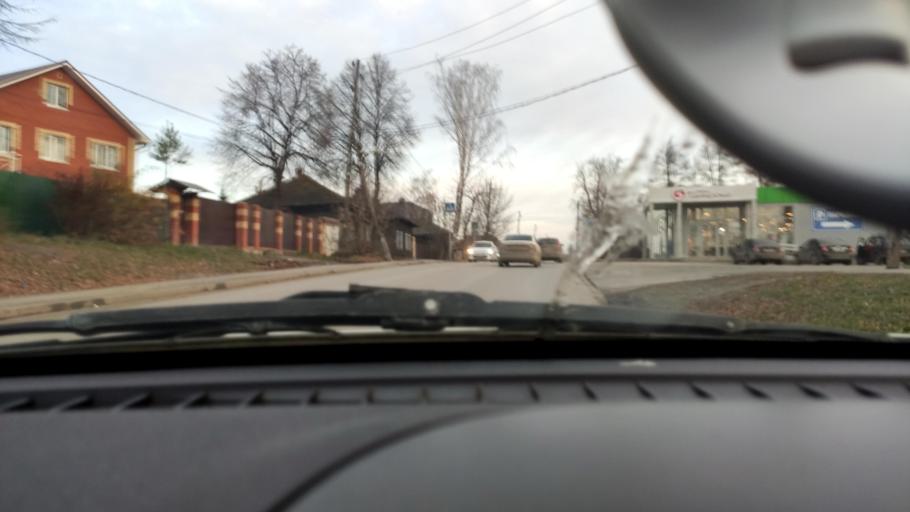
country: RU
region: Perm
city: Perm
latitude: 58.0428
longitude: 56.3271
